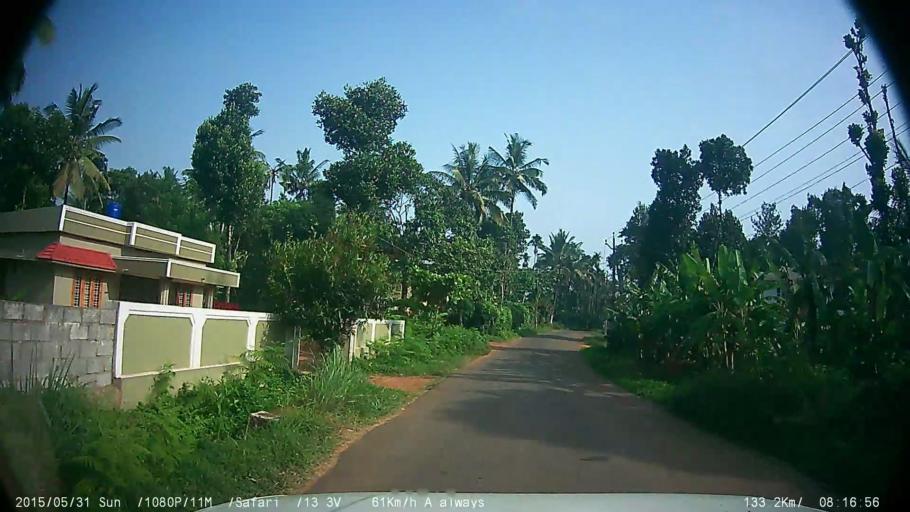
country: IN
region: Kerala
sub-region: Wayanad
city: Kalpetta
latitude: 11.6557
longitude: 75.9927
